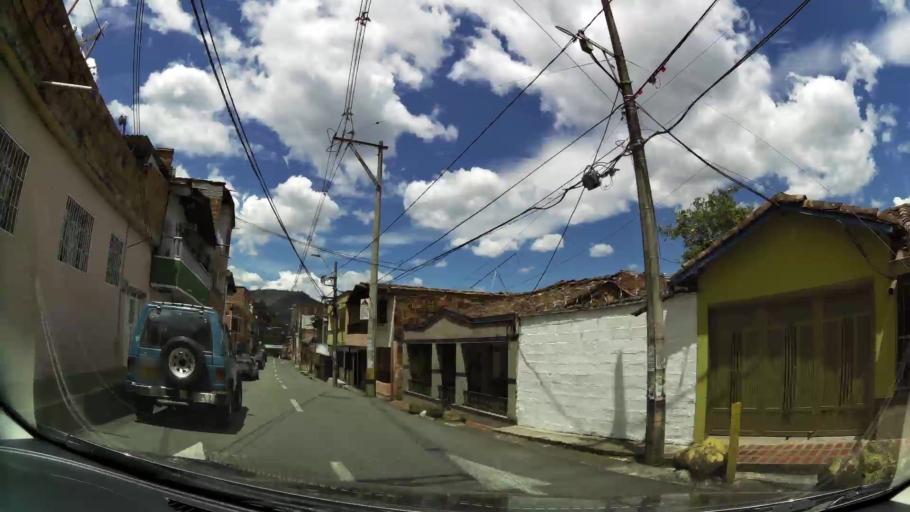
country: CO
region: Antioquia
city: La Estrella
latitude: 6.1567
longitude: -75.6416
